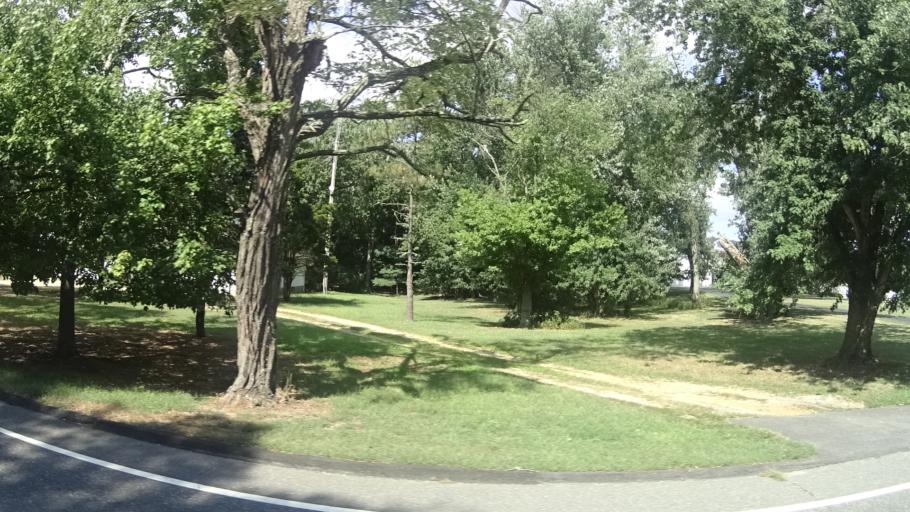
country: US
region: New Jersey
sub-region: Monmouth County
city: Ramtown
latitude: 40.1554
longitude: -74.1156
